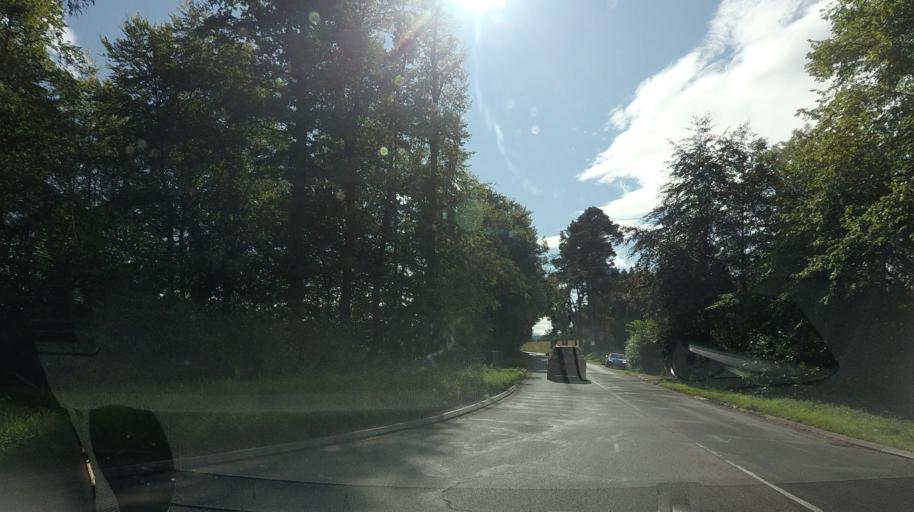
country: GB
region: Scotland
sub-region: Aberdeenshire
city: Banchory
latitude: 57.0811
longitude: -2.5063
